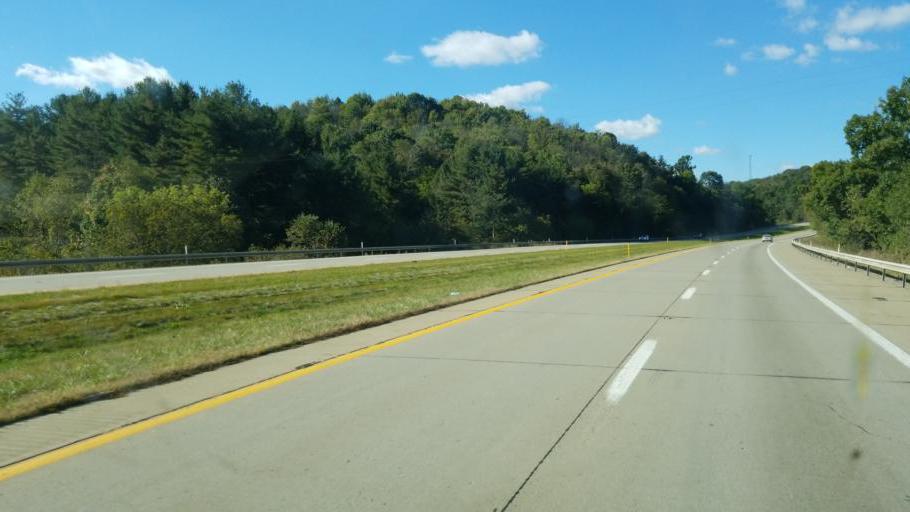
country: US
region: Pennsylvania
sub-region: Greene County
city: Morrisville
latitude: 39.9169
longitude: -80.1619
